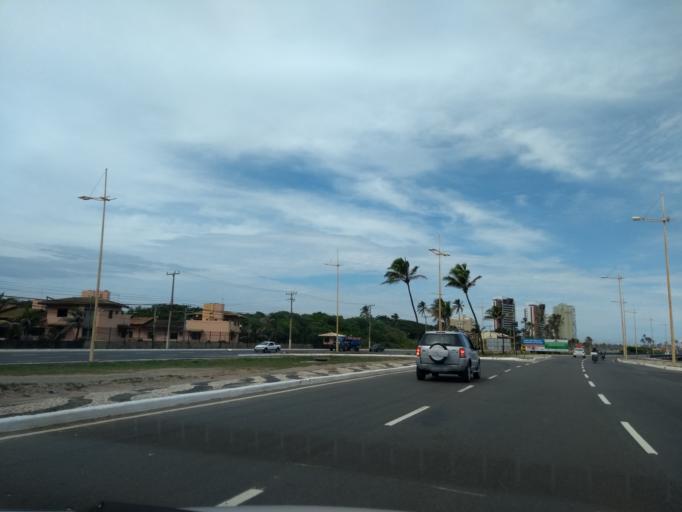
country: BR
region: Bahia
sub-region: Lauro De Freitas
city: Lauro de Freitas
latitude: -12.9628
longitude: -38.4007
